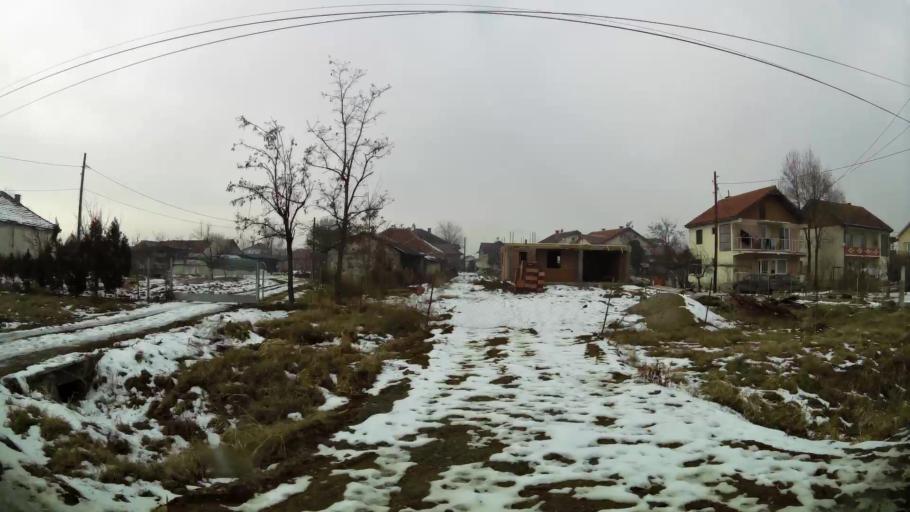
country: MK
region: Ilinden
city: Ilinden
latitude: 41.9932
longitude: 21.5733
